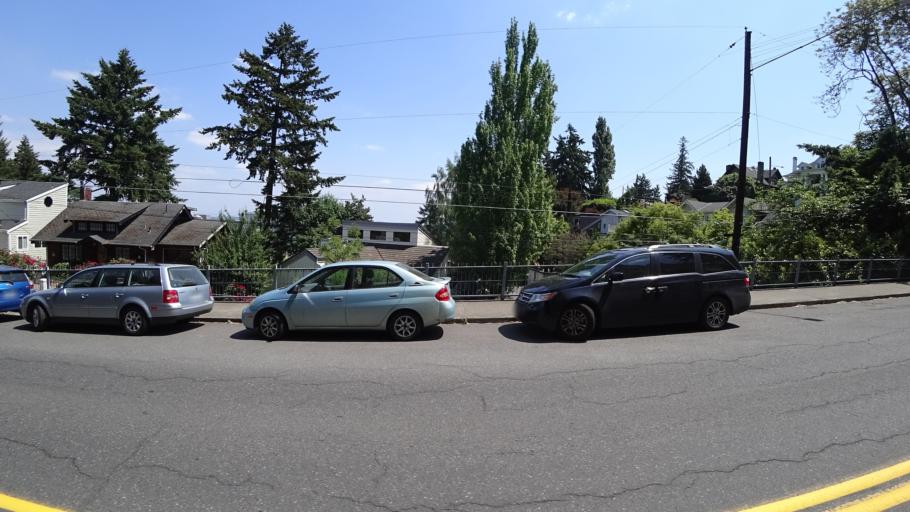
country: US
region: Oregon
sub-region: Multnomah County
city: Portland
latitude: 45.5154
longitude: -122.6972
